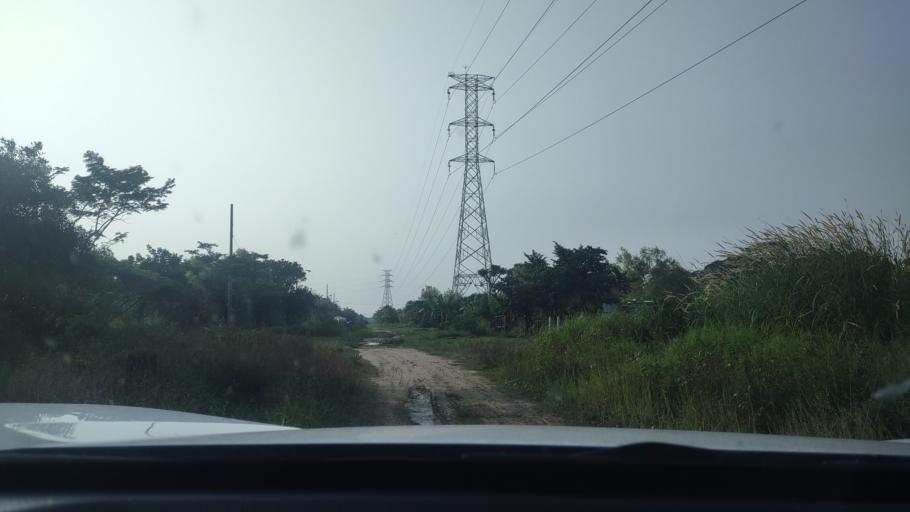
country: MX
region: Veracruz
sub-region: Coatzacoalcos
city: Centro de Readaptacion Social
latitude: 18.1325
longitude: -94.5177
